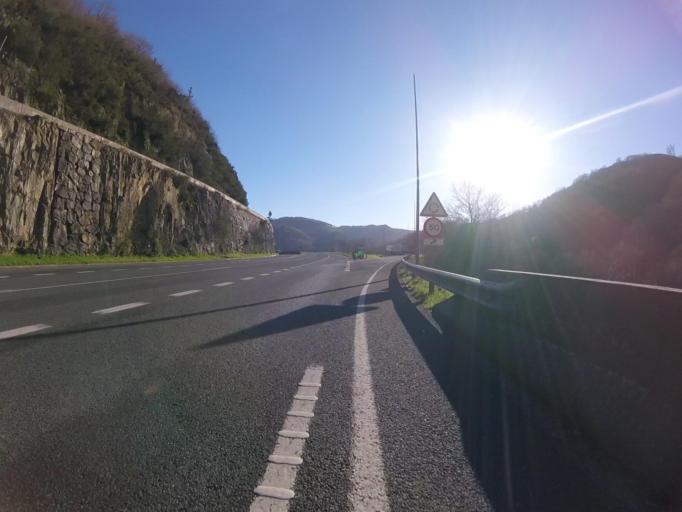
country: ES
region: Navarre
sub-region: Provincia de Navarra
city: Bera
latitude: 43.2840
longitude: -1.7121
